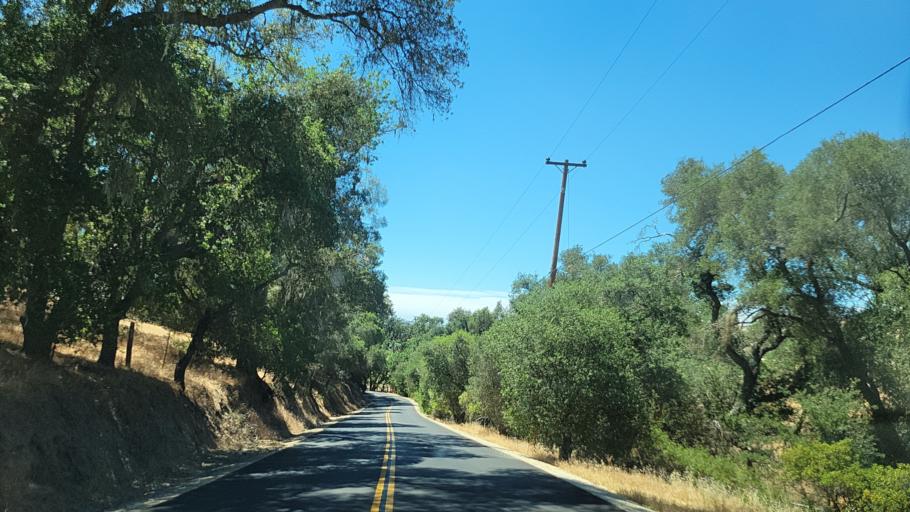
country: US
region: California
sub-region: San Luis Obispo County
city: Atascadero
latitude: 35.4800
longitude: -120.6262
